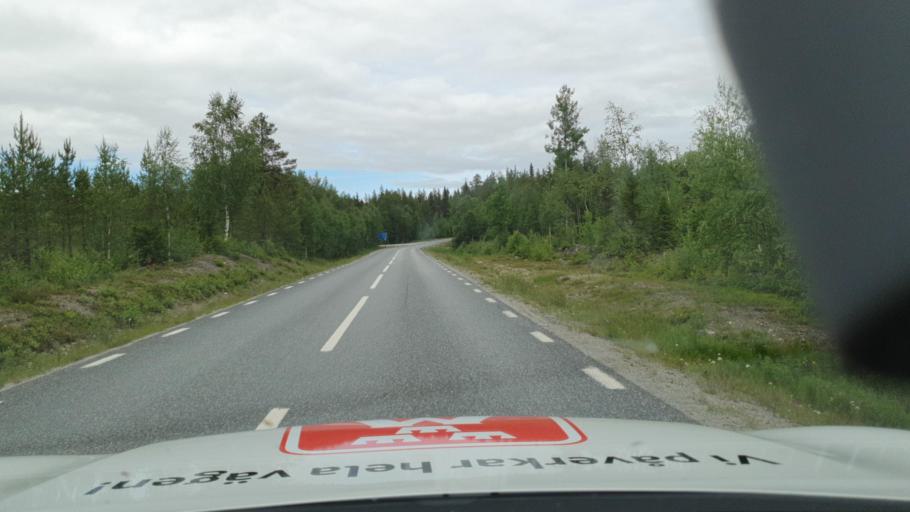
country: SE
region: Vaesterbotten
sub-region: Asele Kommun
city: Insjon
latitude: 64.2535
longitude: 17.5508
